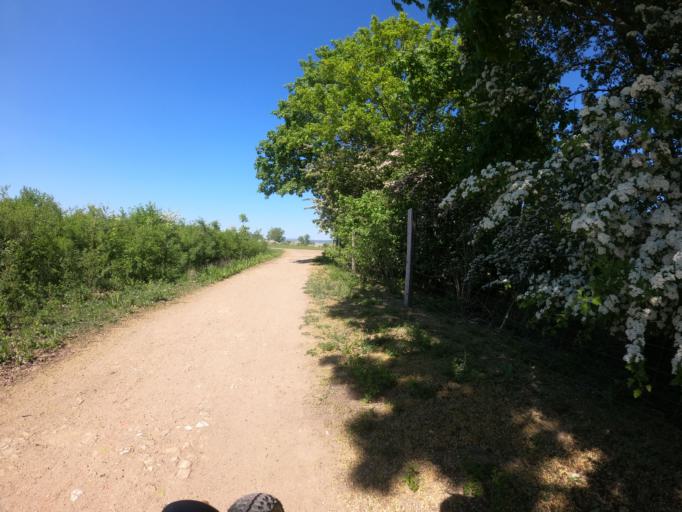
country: DE
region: Hesse
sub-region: Regierungsbezirk Darmstadt
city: Florsheim
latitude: 50.0103
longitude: 8.3967
